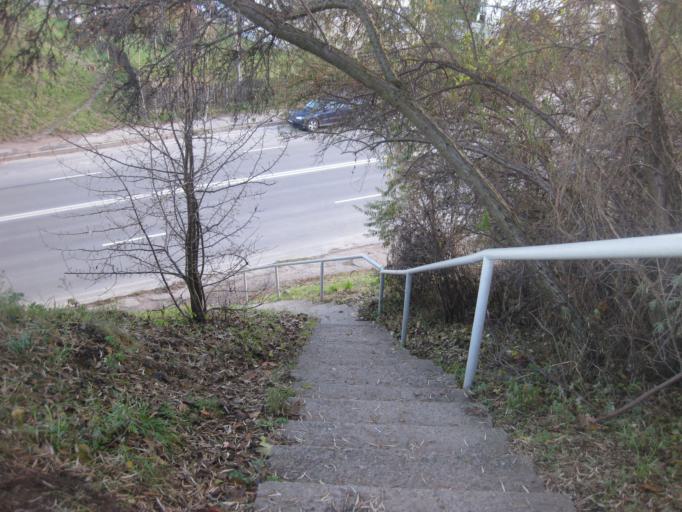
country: LT
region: Kauno apskritis
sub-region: Kaunas
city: Silainiai
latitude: 54.9256
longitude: 23.9042
